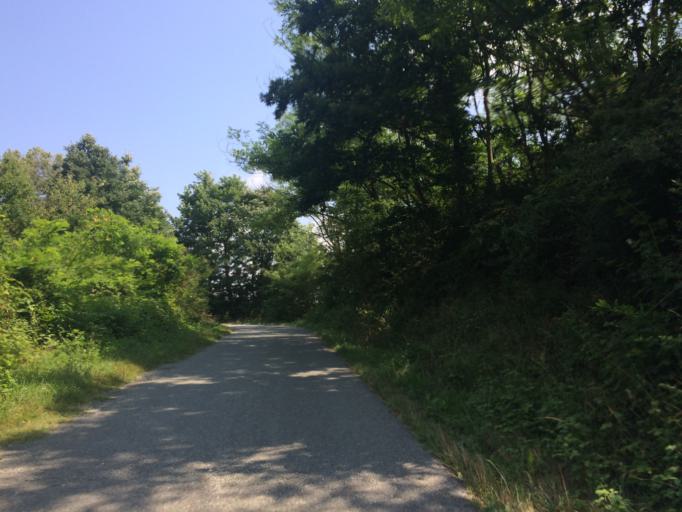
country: IT
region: Piedmont
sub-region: Provincia di Alessandria
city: Pareto
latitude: 44.4914
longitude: 8.3521
